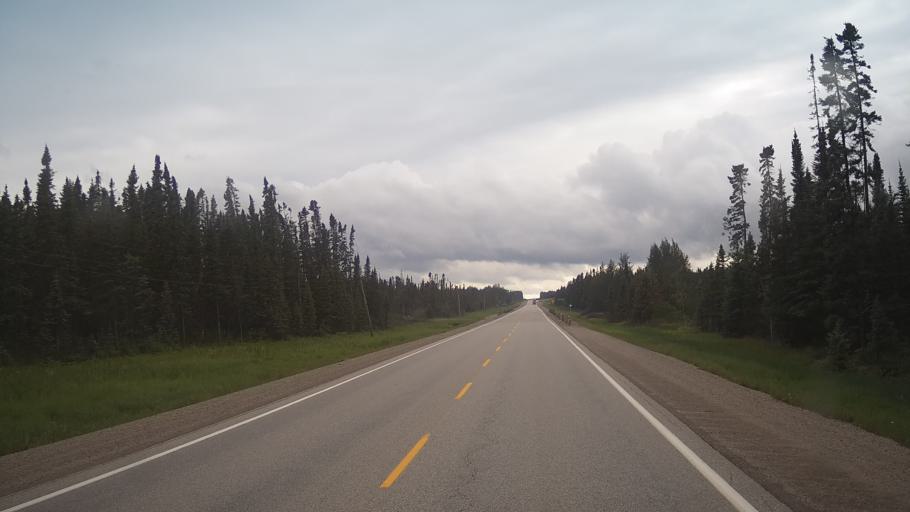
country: CA
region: Ontario
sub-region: Thunder Bay District
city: Thunder Bay
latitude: 48.9430
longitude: -90.1737
